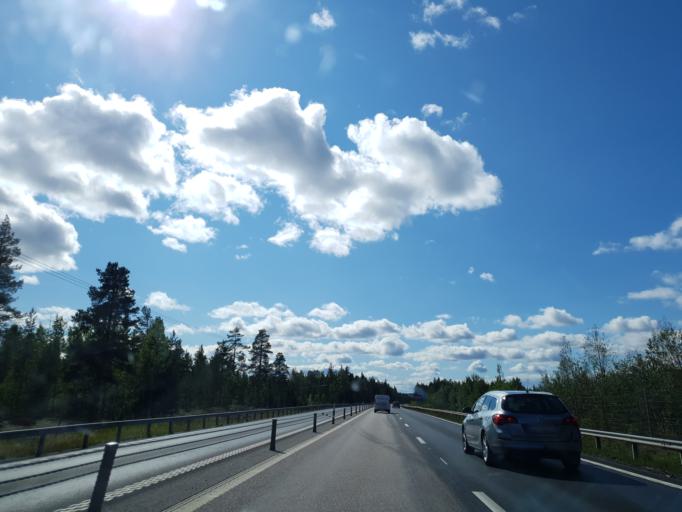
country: SE
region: Vaesterbotten
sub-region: Nordmalings Kommun
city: Nordmaling
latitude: 63.4904
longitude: 19.3142
